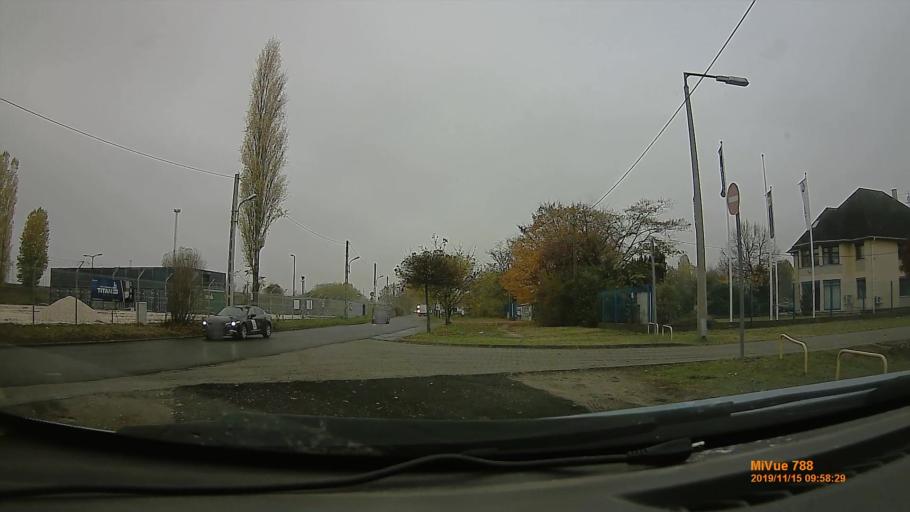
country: HU
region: Budapest
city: Budapest XX. keruelet
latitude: 47.4595
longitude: 19.1022
